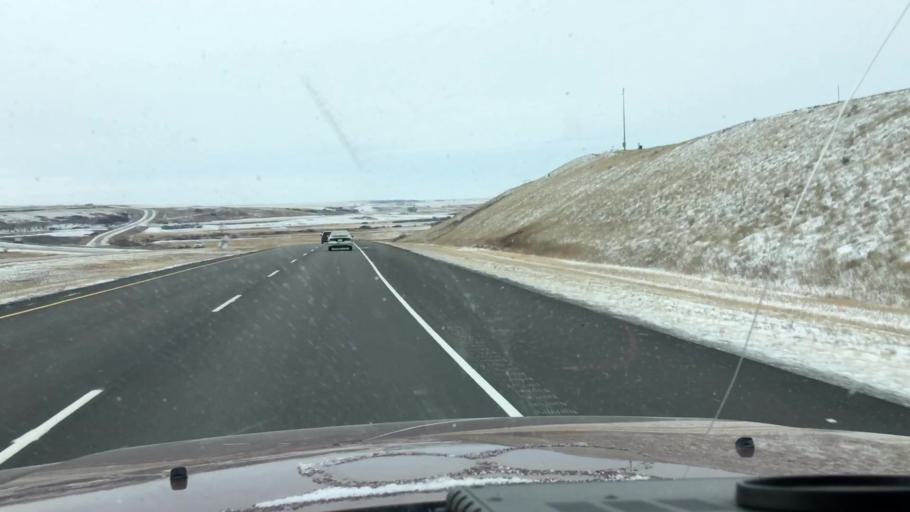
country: CA
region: Saskatchewan
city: Saskatoon
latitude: 51.7374
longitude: -106.4769
